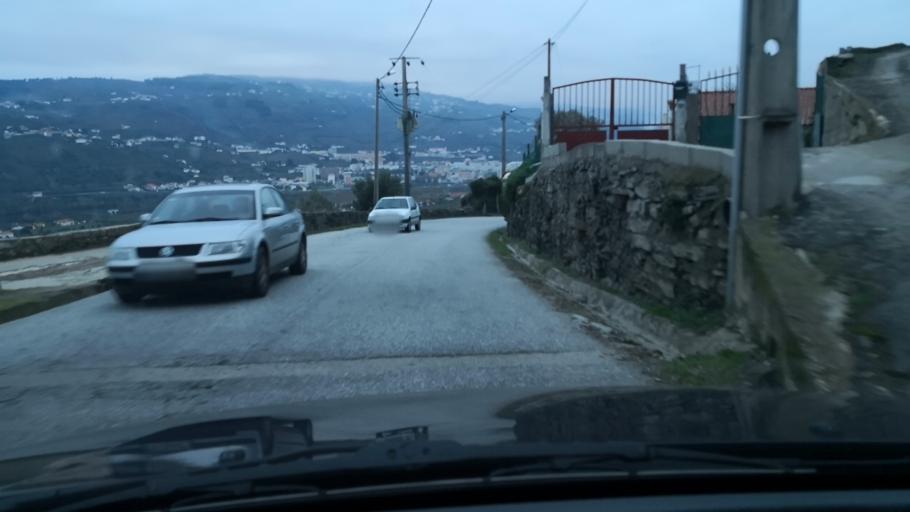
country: PT
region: Vila Real
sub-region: Peso da Regua
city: Peso da Regua
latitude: 41.1459
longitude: -7.7923
